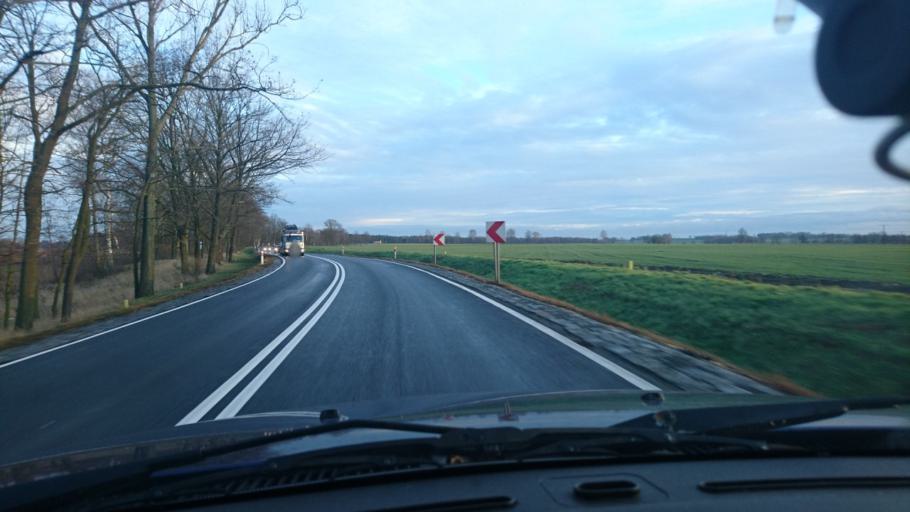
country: PL
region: Lodz Voivodeship
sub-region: Powiat wieruszowski
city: Boleslawiec
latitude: 51.1568
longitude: 18.1694
